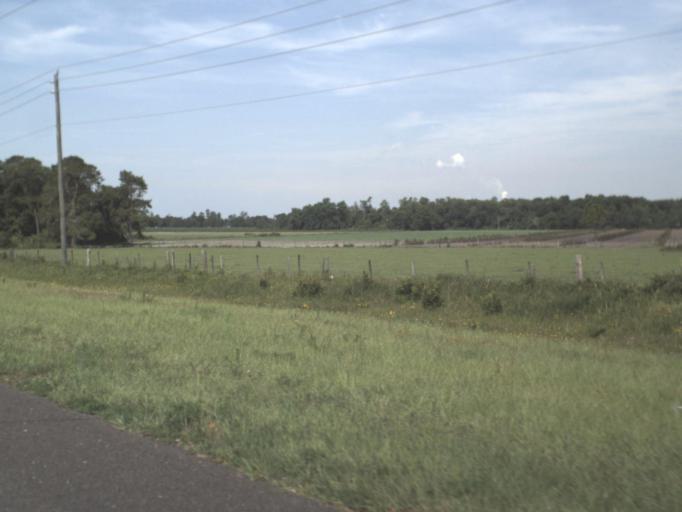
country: US
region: Florida
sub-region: Saint Johns County
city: Saint Augustine Shores
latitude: 29.7599
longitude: -81.4630
